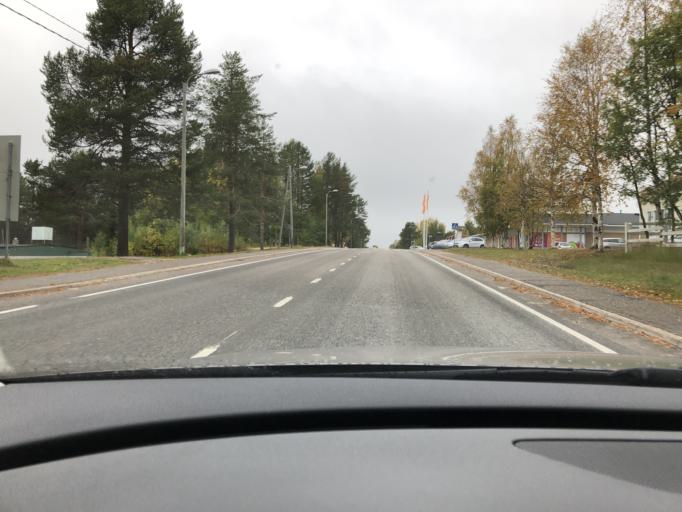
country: FI
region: Lapland
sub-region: Itae-Lappi
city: Posio
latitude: 66.1095
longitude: 28.1735
